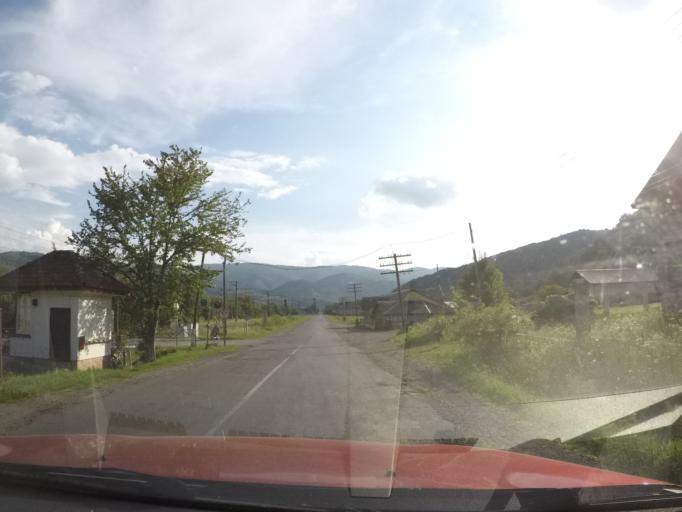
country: UA
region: Zakarpattia
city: Velykyi Bereznyi
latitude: 48.9511
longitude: 22.6078
